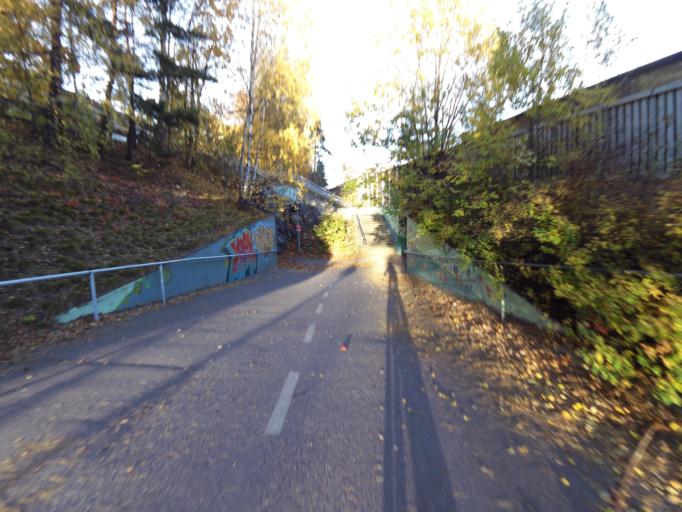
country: FI
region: Uusimaa
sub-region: Helsinki
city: Vantaa
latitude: 60.1993
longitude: 25.0366
